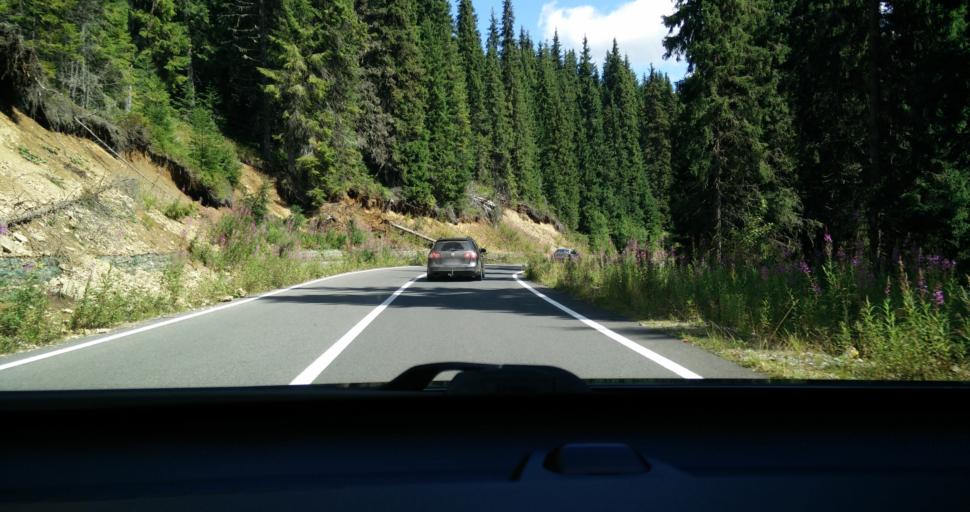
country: RO
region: Hunedoara
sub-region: Oras Petrila
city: Petrila
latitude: 45.5023
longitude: 23.6400
